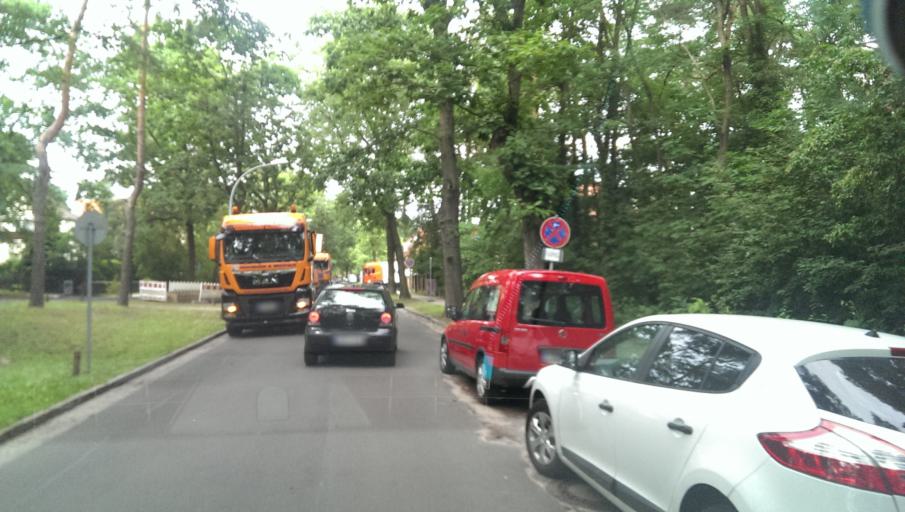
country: DE
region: Brandenburg
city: Kleinmachnow
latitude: 52.4123
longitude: 13.2237
